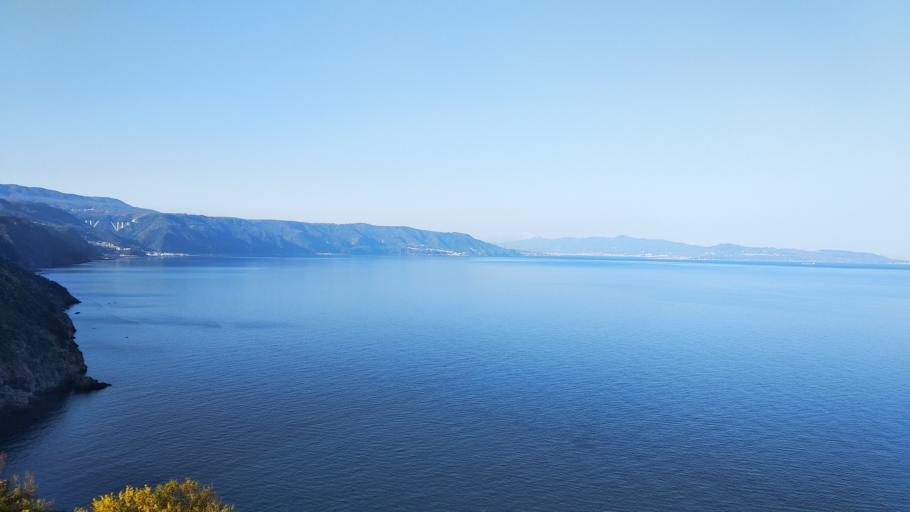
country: IT
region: Calabria
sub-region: Provincia di Reggio Calabria
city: Seminara
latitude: 38.3559
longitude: 15.8351
